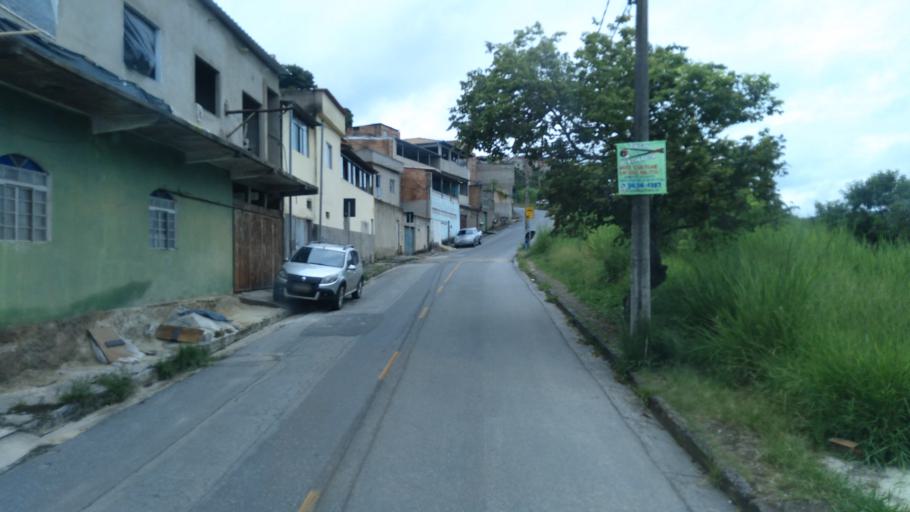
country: BR
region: Minas Gerais
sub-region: Santa Luzia
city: Santa Luzia
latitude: -19.8324
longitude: -43.8672
